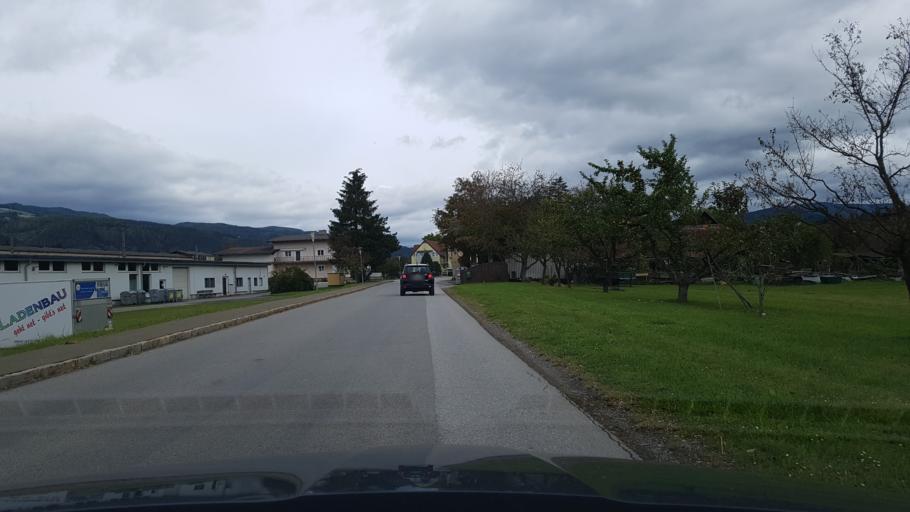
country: AT
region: Styria
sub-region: Politischer Bezirk Bruck-Muerzzuschlag
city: Sankt Marein im Muerztal
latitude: 47.4707
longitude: 15.3692
